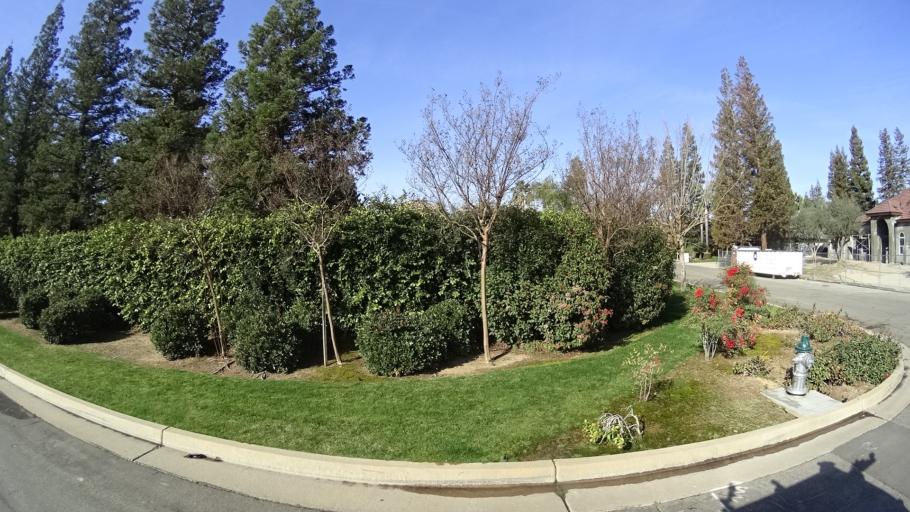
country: US
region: California
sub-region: Fresno County
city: Clovis
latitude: 36.8813
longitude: -119.7664
